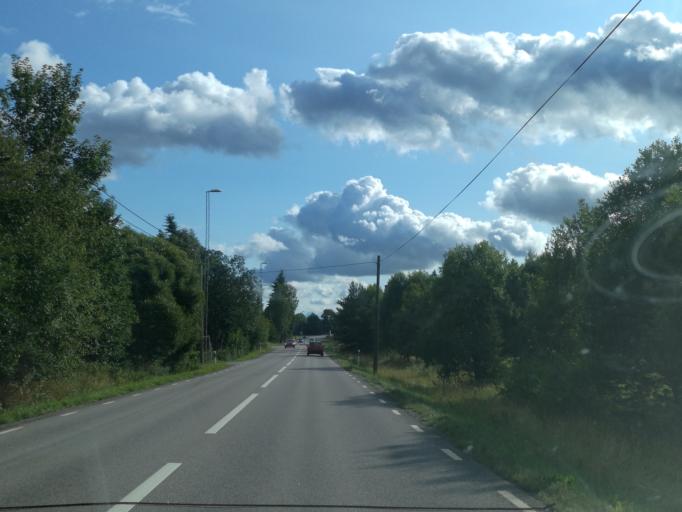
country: SE
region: Stockholm
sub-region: Upplands Vasby Kommun
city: Upplands Vaesby
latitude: 59.5287
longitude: 17.9658
